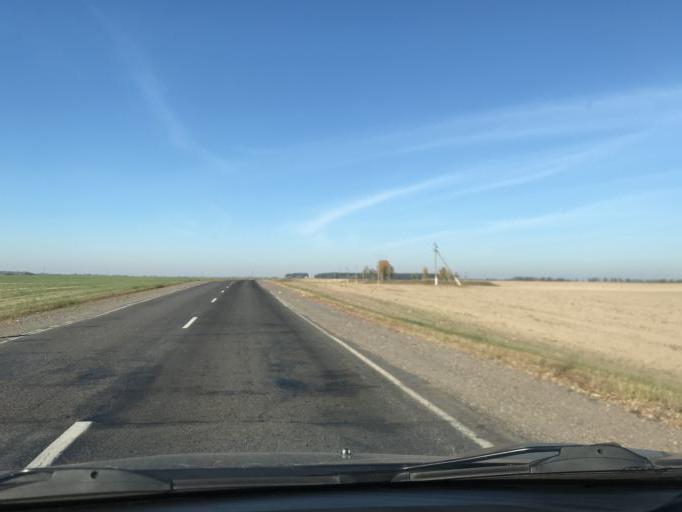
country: BY
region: Gomel
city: Brahin
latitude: 51.8010
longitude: 30.1279
